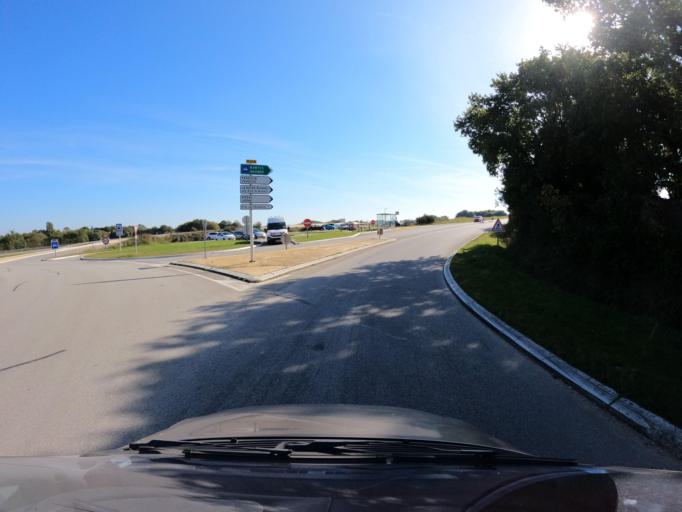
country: FR
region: Brittany
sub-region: Departement du Morbihan
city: Peaule
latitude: 47.5389
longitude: -2.3985
